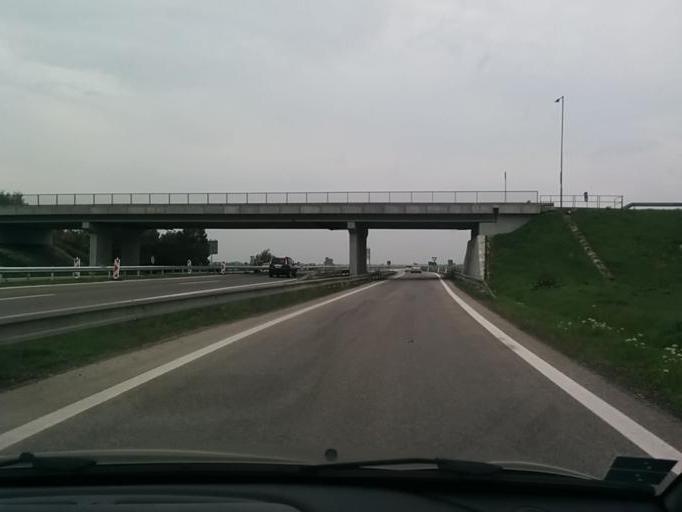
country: SK
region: Trnavsky
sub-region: Okres Trnava
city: Trnava
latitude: 48.3493
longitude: 17.6194
